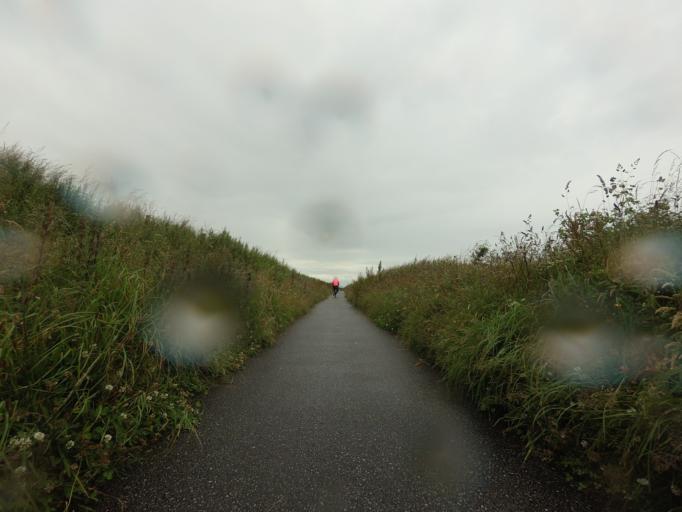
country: GB
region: Scotland
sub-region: Moray
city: Findochty
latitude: 57.6901
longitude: -2.9169
